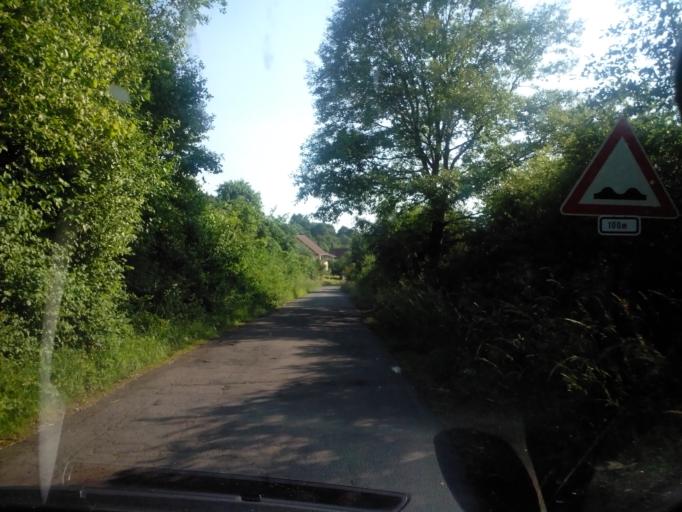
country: DE
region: Saarland
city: Nalbach
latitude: 49.4196
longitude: 6.7737
